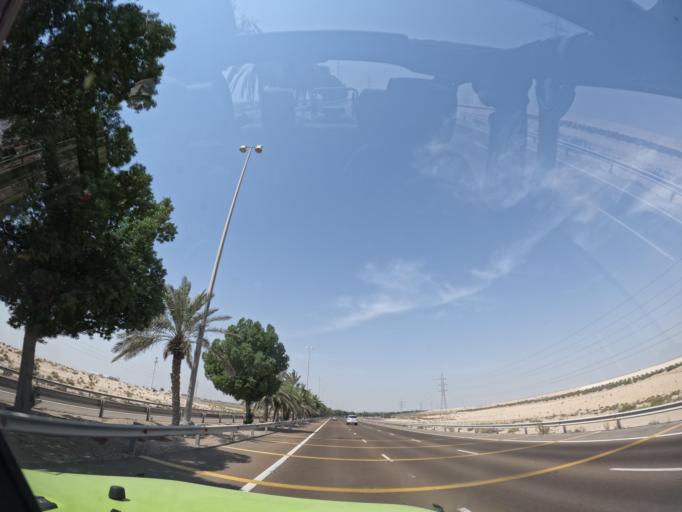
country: AE
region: Abu Dhabi
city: Abu Dhabi
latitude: 24.2326
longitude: 54.7649
